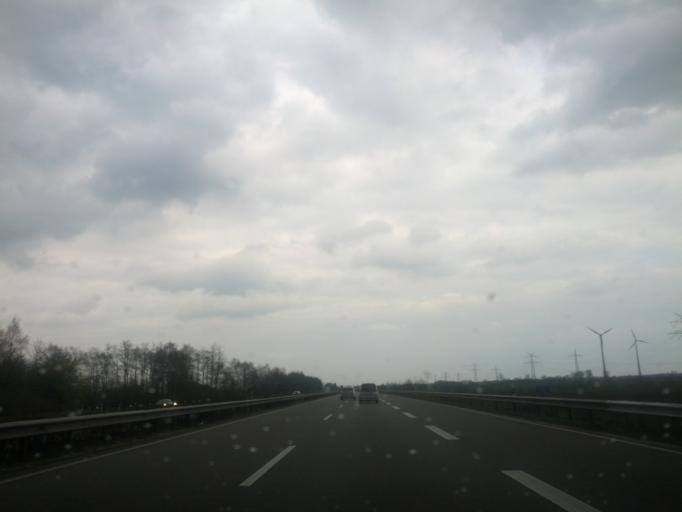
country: DE
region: Lower Saxony
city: Apen
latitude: 53.2600
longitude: 7.7583
